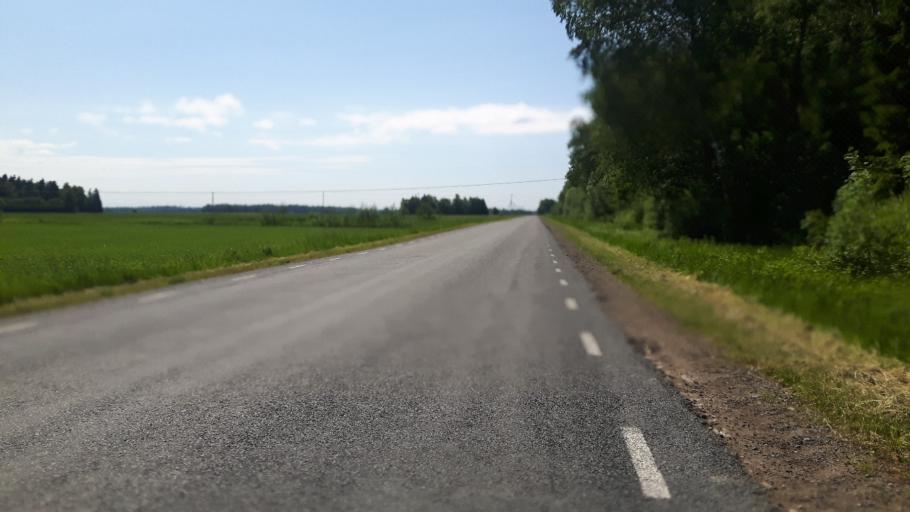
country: EE
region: Paernumaa
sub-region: Vaendra vald (alev)
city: Vandra
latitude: 58.6298
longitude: 25.0208
